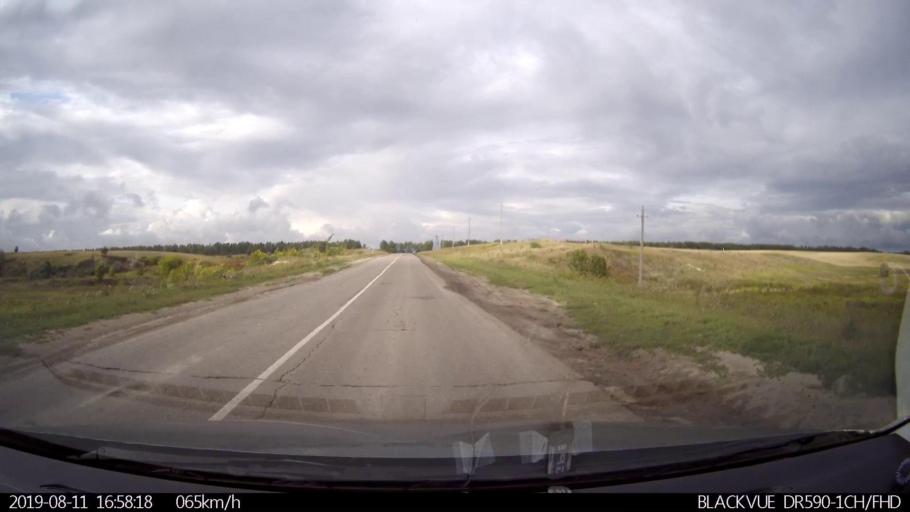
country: RU
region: Ulyanovsk
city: Mayna
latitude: 54.3070
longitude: 47.6557
